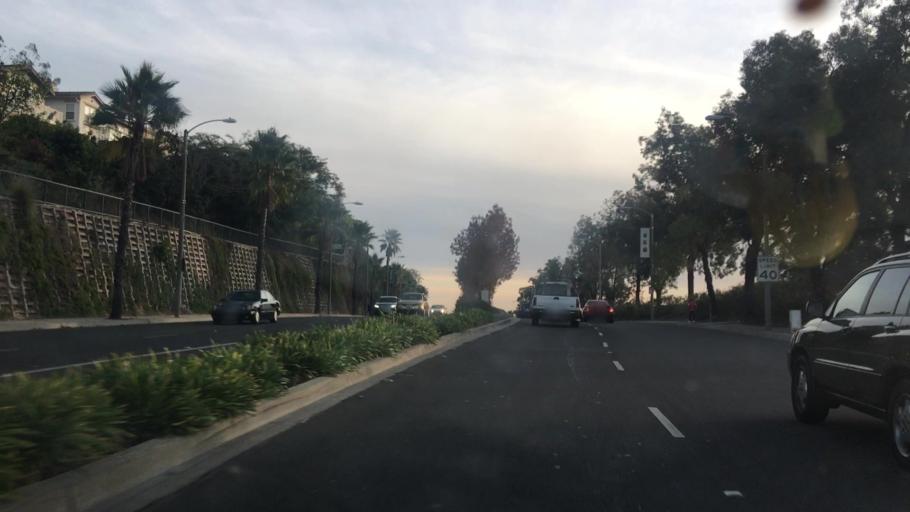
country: US
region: California
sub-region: Los Angeles County
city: Signal Hill
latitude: 33.8002
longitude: -118.1677
